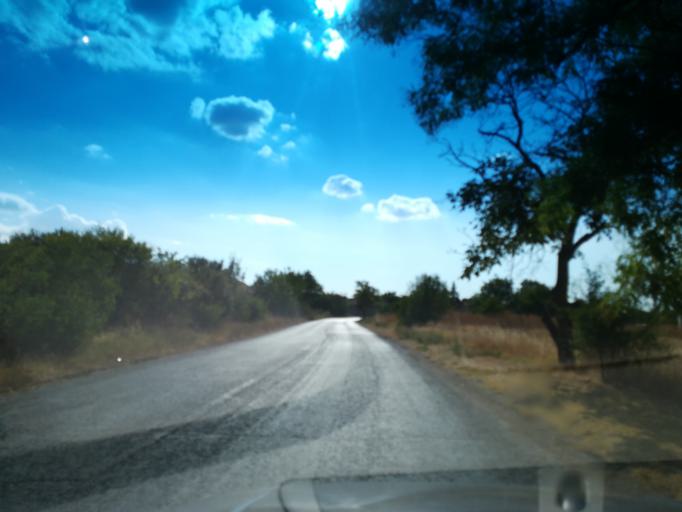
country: BG
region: Khaskovo
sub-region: Obshtina Mineralni Bani
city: Mineralni Bani
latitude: 42.0166
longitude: 25.4295
